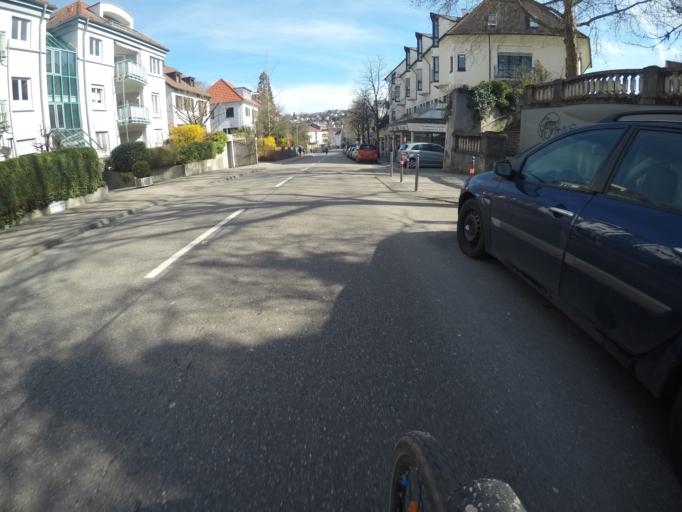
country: DE
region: Baden-Wuerttemberg
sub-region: Regierungsbezirk Stuttgart
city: Stuttgart Feuerbach
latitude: 48.8092
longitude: 9.1544
